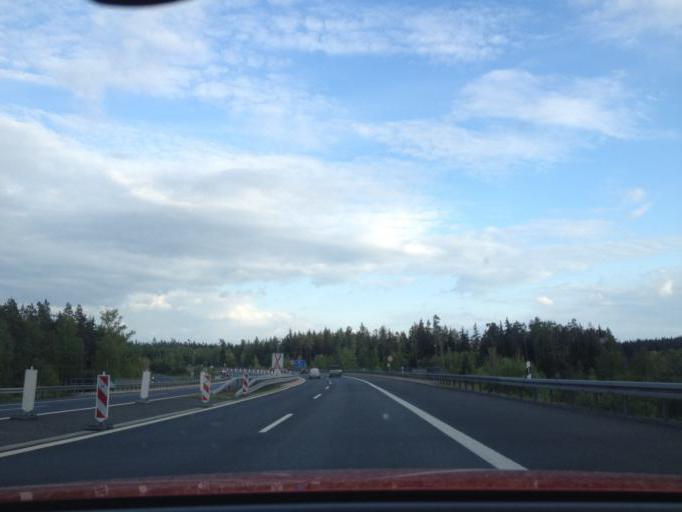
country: DE
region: Bavaria
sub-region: Upper Palatinate
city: Pechbrunn
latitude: 49.9573
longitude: 12.1924
